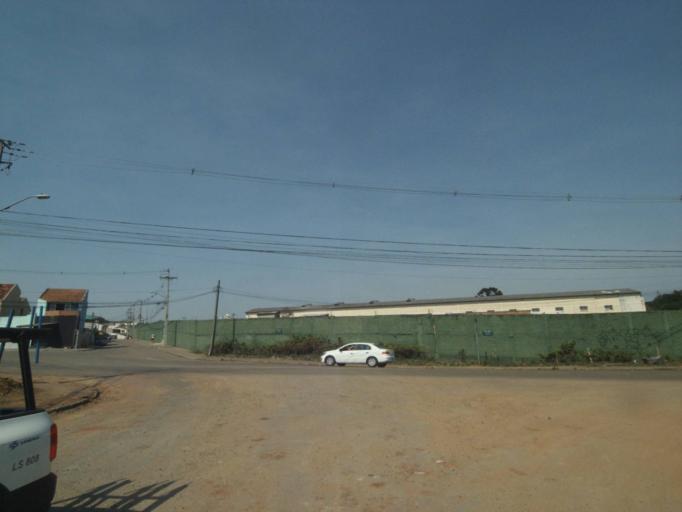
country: BR
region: Parana
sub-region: Curitiba
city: Curitiba
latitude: -25.4826
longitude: -49.3053
